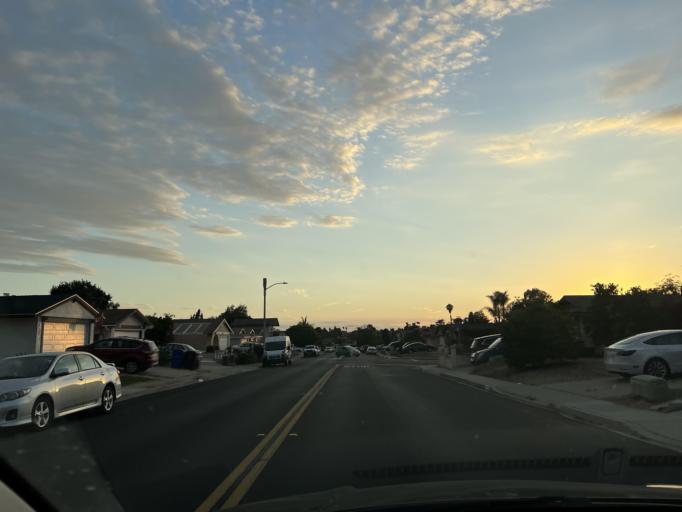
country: US
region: California
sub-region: San Diego County
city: Fairbanks Ranch
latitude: 32.9075
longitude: -117.1500
